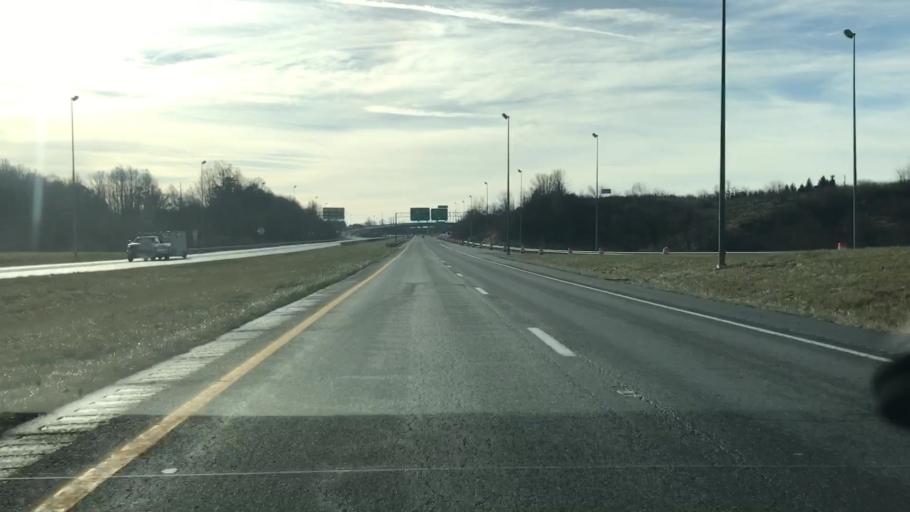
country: US
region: Virginia
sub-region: Montgomery County
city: Merrimac
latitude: 37.1628
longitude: -80.4143
